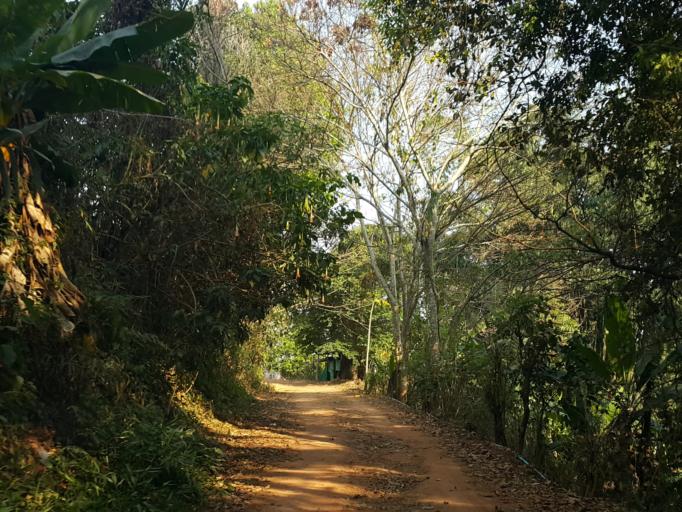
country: TH
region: Chiang Mai
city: Samoeng
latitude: 18.9055
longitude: 98.7968
